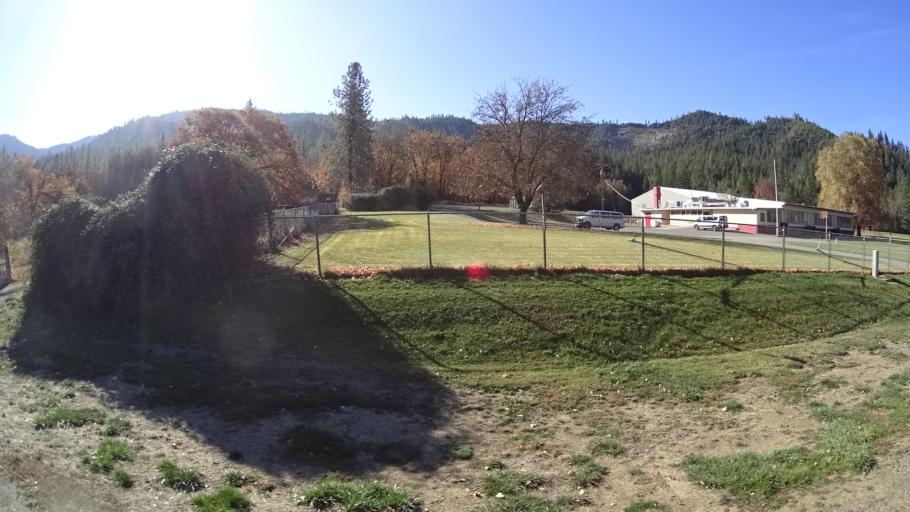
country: US
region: California
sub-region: Siskiyou County
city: Yreka
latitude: 41.8227
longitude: -122.9681
